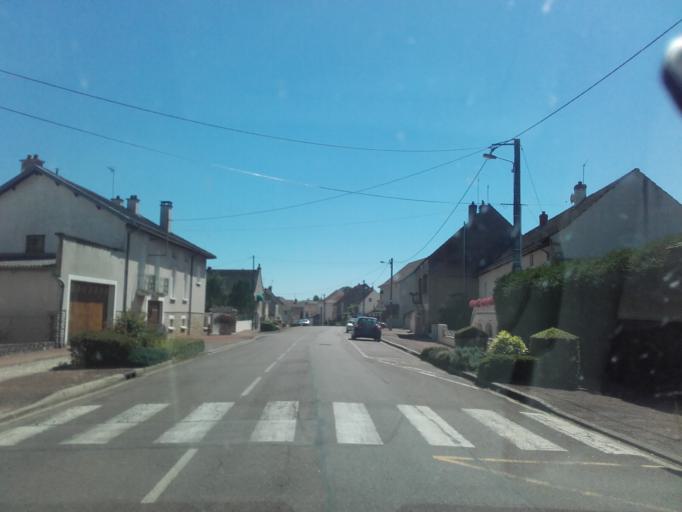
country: FR
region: Bourgogne
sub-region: Departement de la Cote-d'Or
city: Corpeau
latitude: 46.9300
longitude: 4.7528
